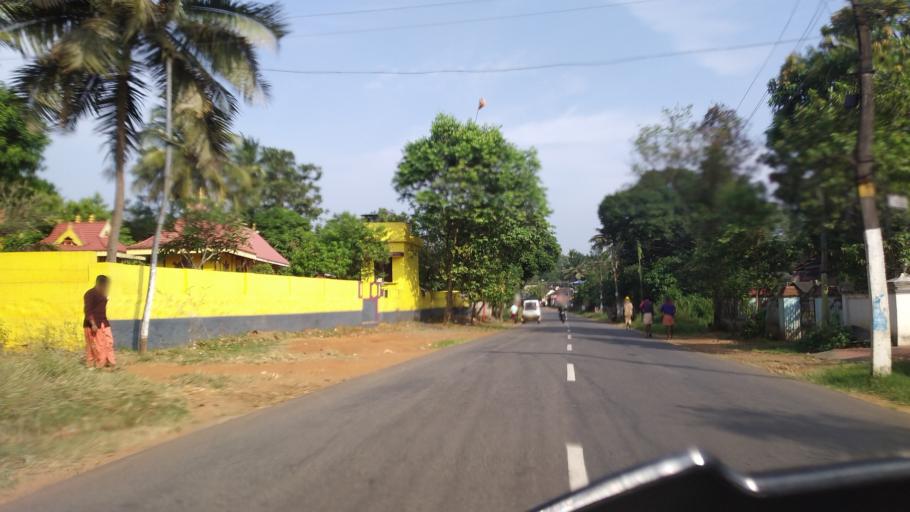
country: IN
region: Kerala
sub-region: Thrissur District
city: Chelakara
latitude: 10.5974
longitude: 76.5282
